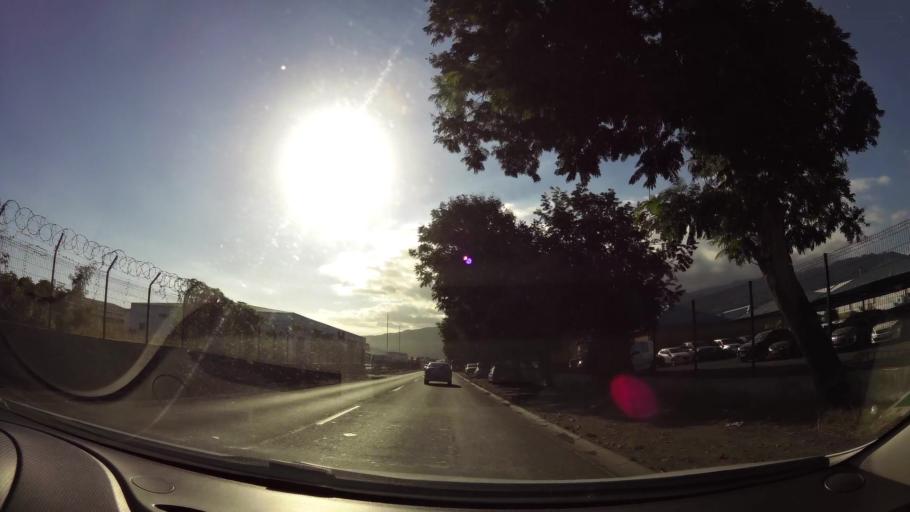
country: RE
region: Reunion
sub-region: Reunion
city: Saint-Louis
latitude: -21.2900
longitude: 55.3997
